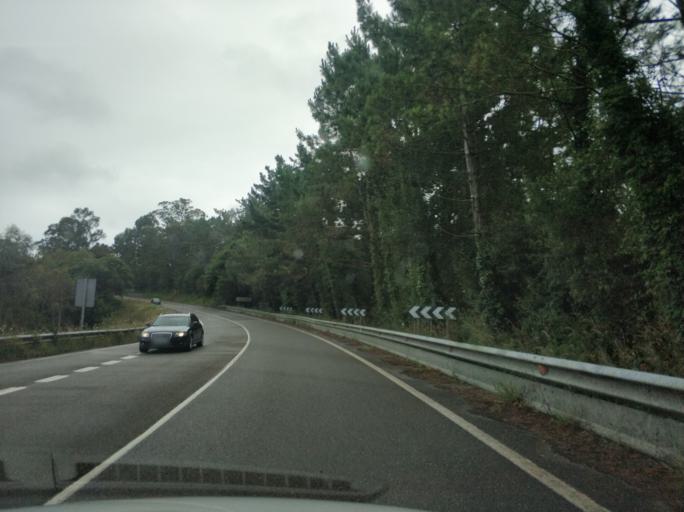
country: ES
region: Asturias
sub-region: Province of Asturias
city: Salas
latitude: 43.5428
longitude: -6.4064
